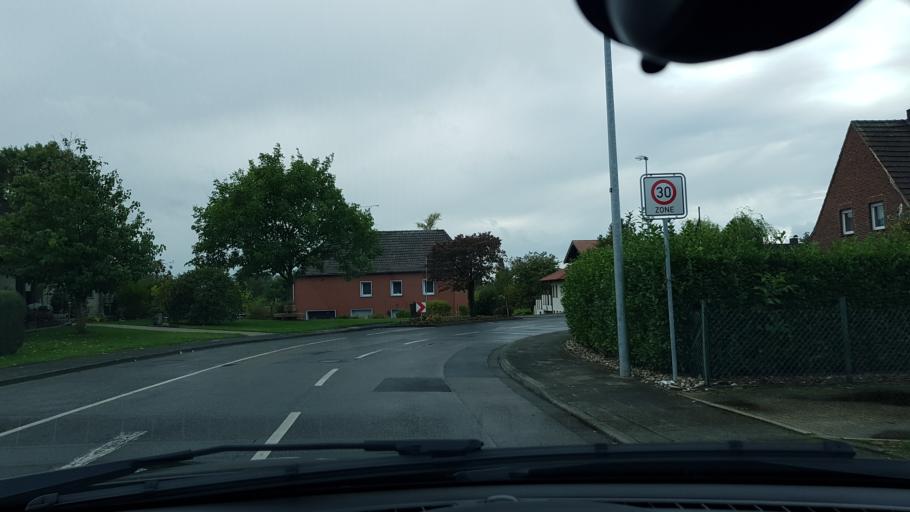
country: DE
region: North Rhine-Westphalia
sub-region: Regierungsbezirk Koln
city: Wassenberg
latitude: 51.0850
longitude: 6.1545
